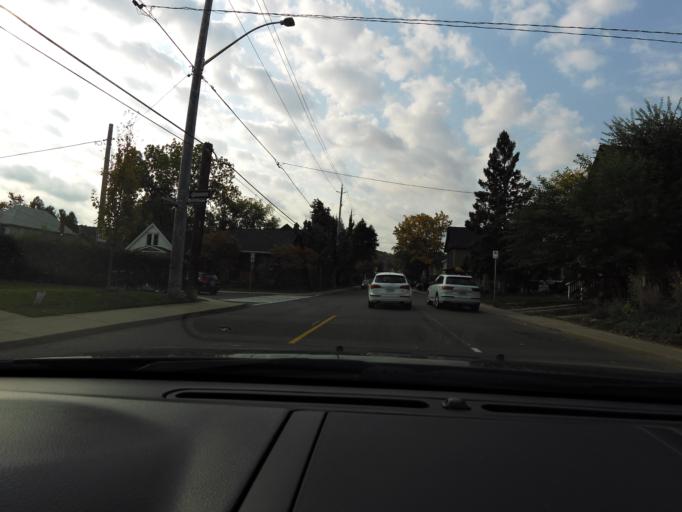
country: CA
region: Ontario
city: Hamilton
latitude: 43.2532
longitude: -79.8813
